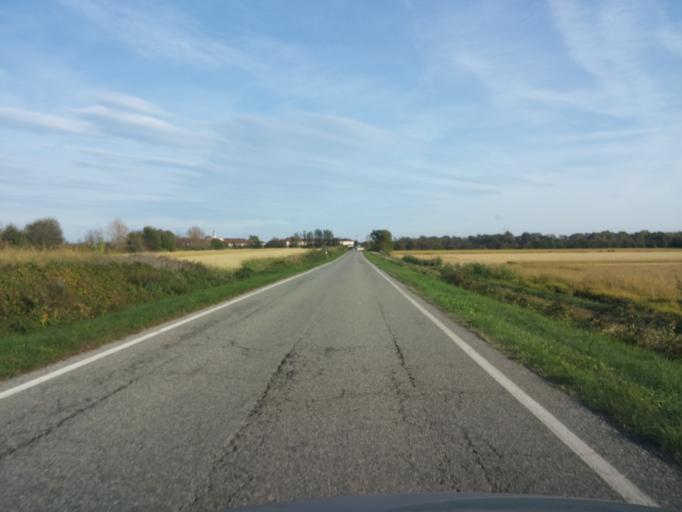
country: IT
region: Piedmont
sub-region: Provincia di Vercelli
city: Carisio
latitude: 45.4332
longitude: 8.1702
